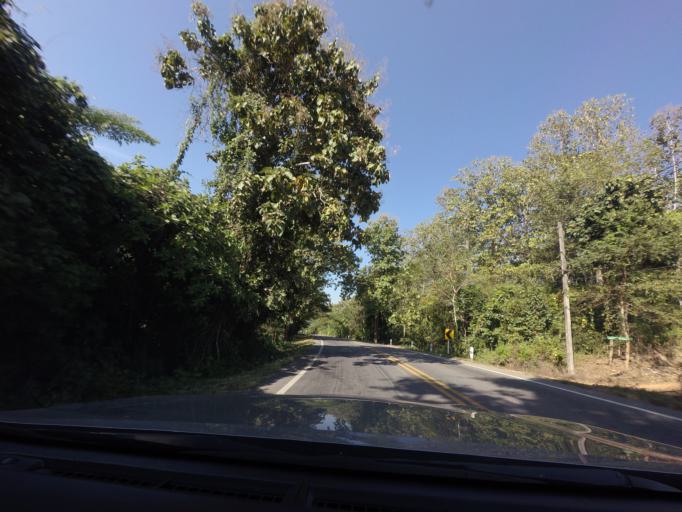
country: TH
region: Sukhothai
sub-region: Amphoe Si Satchanalai
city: Si Satchanalai
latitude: 17.6152
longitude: 99.7091
